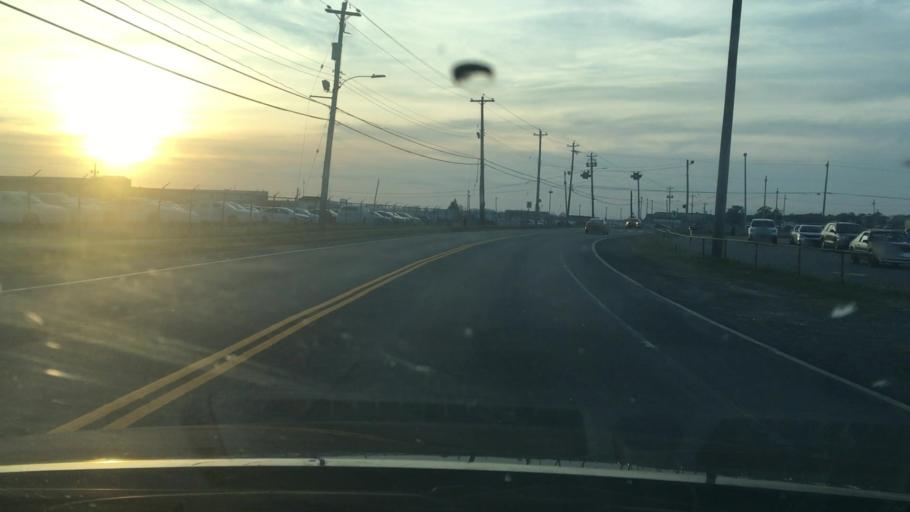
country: CA
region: Nova Scotia
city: Cole Harbour
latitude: 44.6205
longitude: -63.5060
